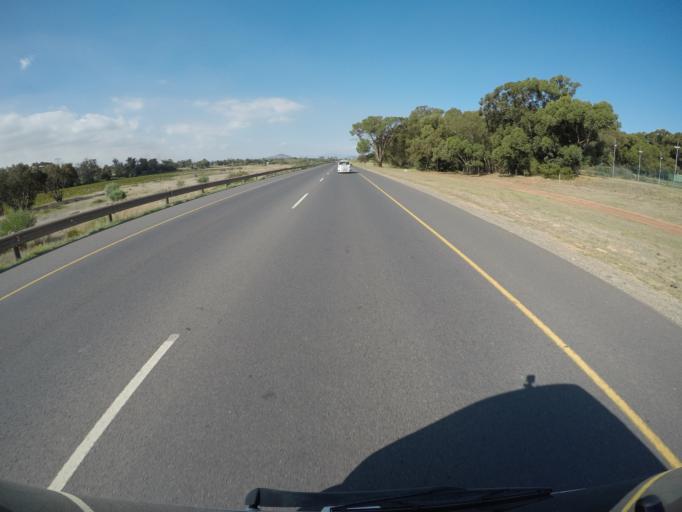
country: ZA
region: Western Cape
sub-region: City of Cape Town
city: Kraaifontein
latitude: -33.8836
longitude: 18.7529
